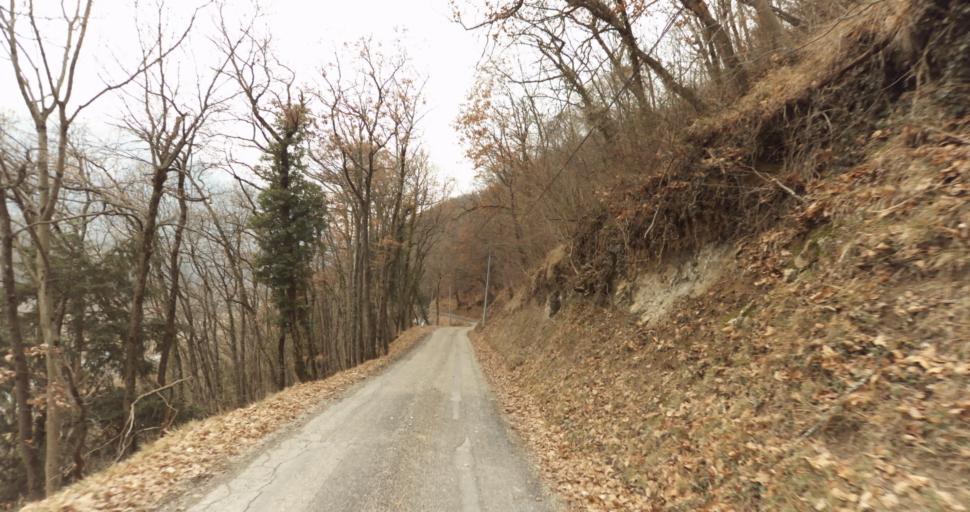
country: FR
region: Rhone-Alpes
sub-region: Departement de l'Isere
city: Saint-Georges-de-Commiers
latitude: 45.0378
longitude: 5.6910
